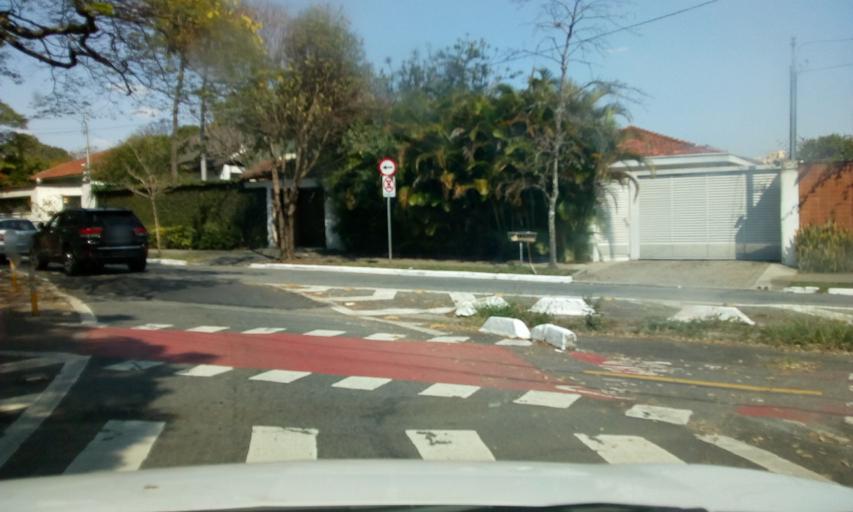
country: BR
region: Sao Paulo
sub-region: Osasco
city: Osasco
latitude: -23.5260
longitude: -46.7191
